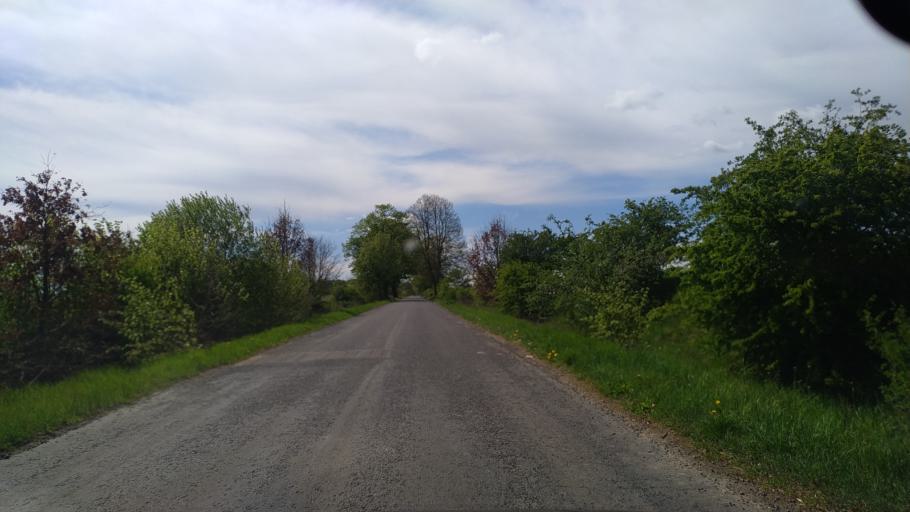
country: PL
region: West Pomeranian Voivodeship
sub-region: Powiat walecki
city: Walcz
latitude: 53.3541
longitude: 16.3013
